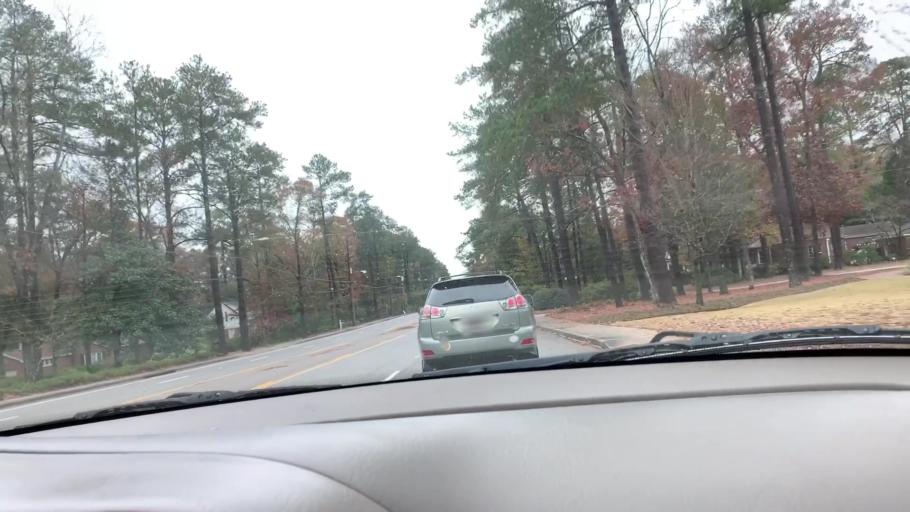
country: US
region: South Carolina
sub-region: Richland County
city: Forest Acres
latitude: 34.0287
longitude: -80.9664
